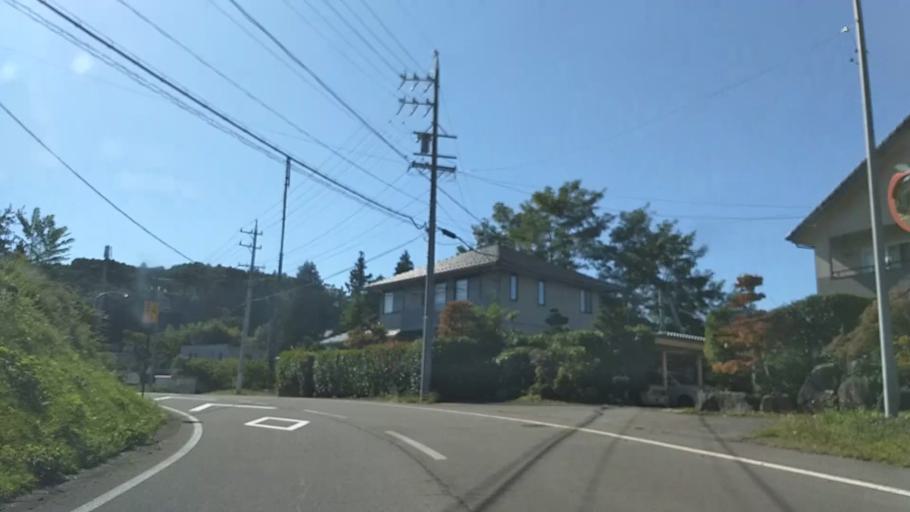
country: JP
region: Nagano
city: Nagano-shi
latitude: 36.5851
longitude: 138.1113
